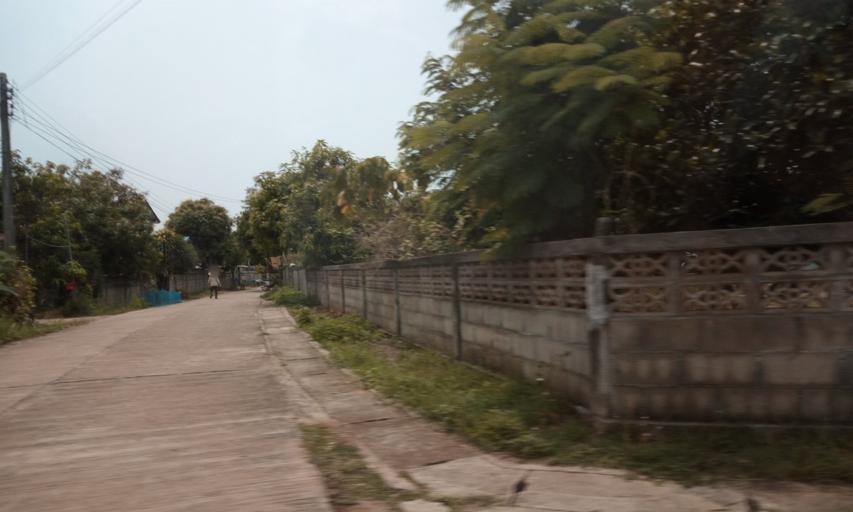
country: TH
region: Phayao
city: Phu Sang
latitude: 19.6139
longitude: 100.3255
